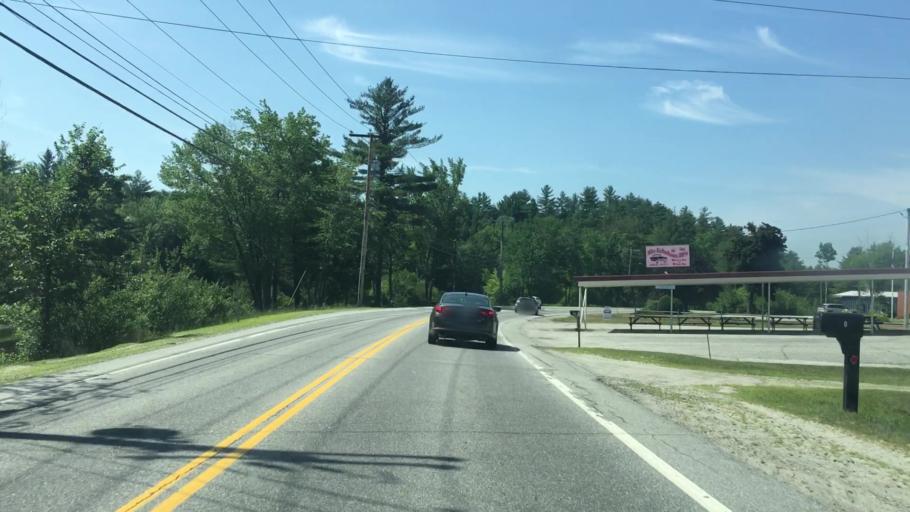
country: US
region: New Hampshire
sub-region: Sullivan County
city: Newport
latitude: 43.3737
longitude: -72.1569
